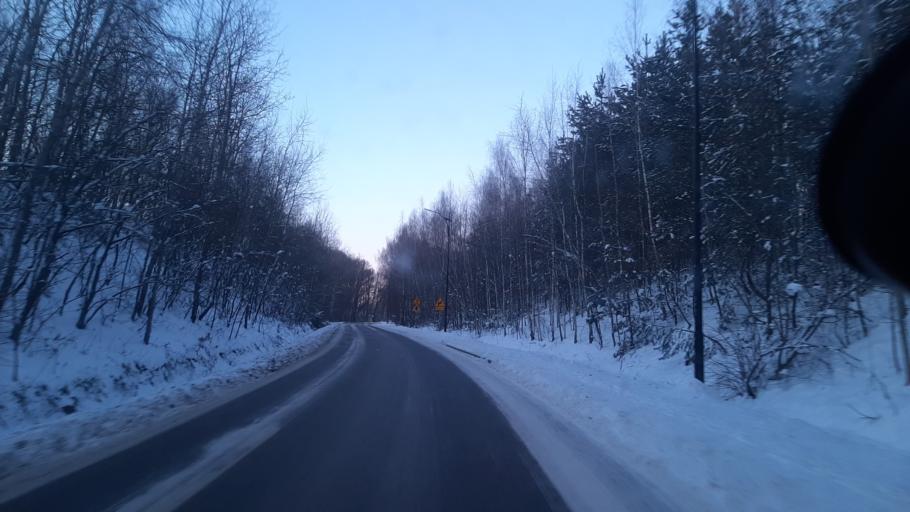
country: PL
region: Lublin Voivodeship
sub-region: Powiat lubelski
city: Lublin
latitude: 51.3187
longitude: 22.5615
